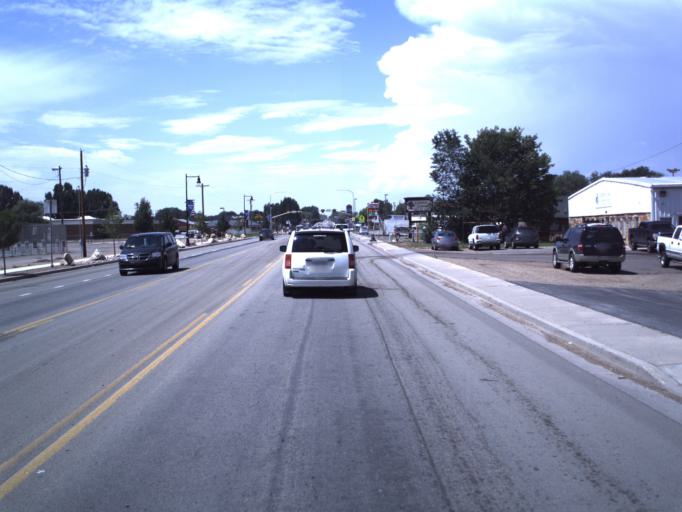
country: US
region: Utah
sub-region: Duchesne County
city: Roosevelt
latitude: 40.3023
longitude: -109.9736
